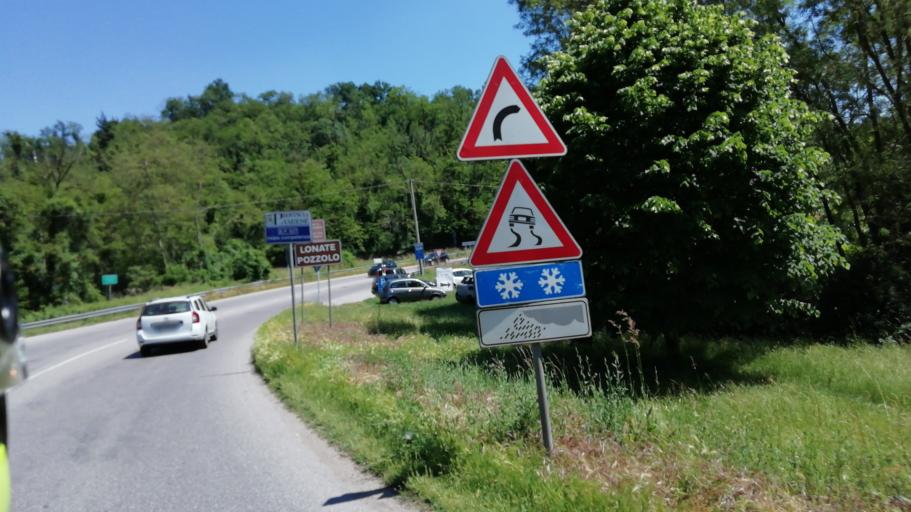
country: IT
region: Lombardy
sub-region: Provincia di Varese
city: Vizzola Ticino
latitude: 45.5894
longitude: 8.7057
